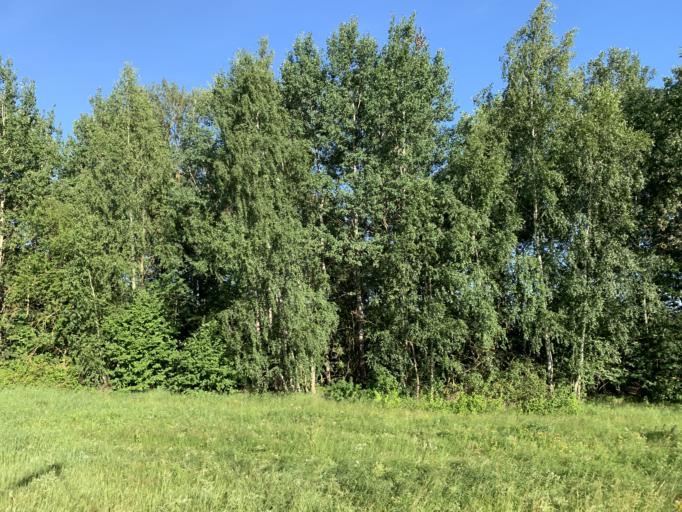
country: BY
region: Minsk
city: Novy Svyerzhan'
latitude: 53.4136
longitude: 26.6453
